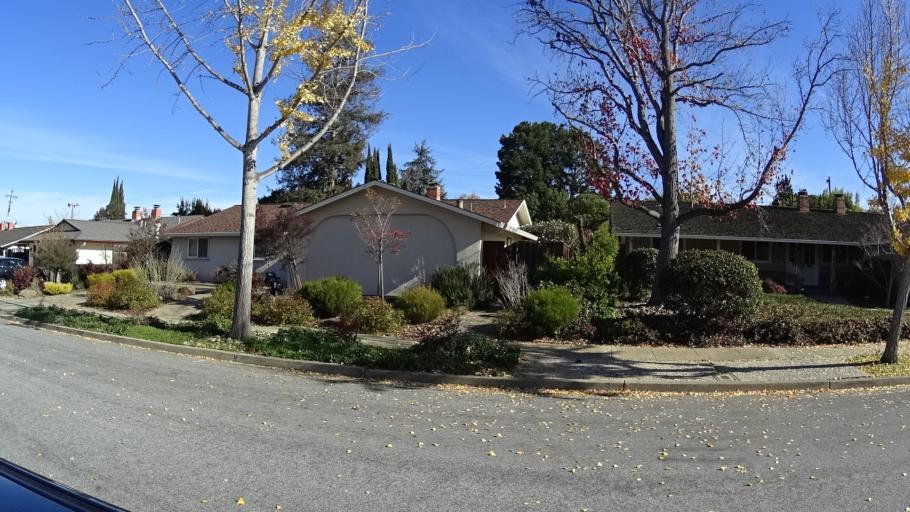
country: US
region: California
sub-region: Santa Clara County
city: Sunnyvale
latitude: 37.3473
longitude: -122.0425
